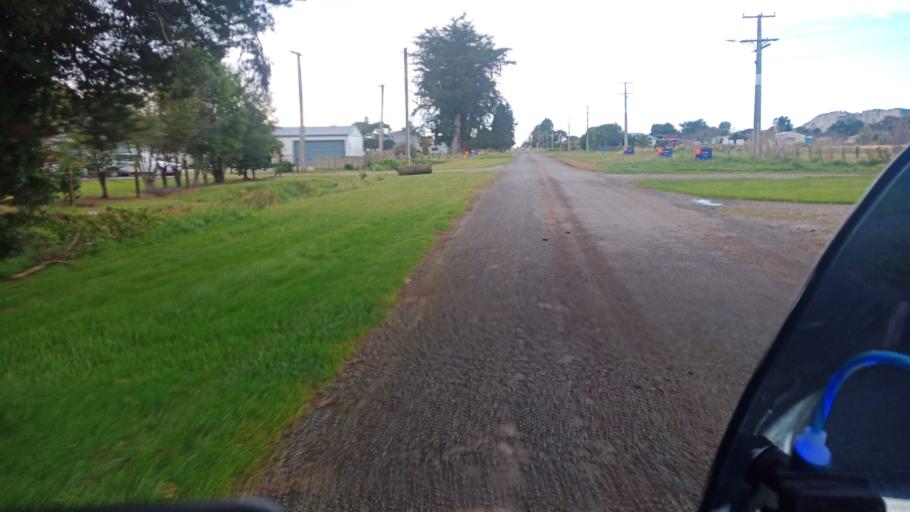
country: NZ
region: Gisborne
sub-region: Gisborne District
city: Gisborne
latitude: -38.3697
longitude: 178.2887
